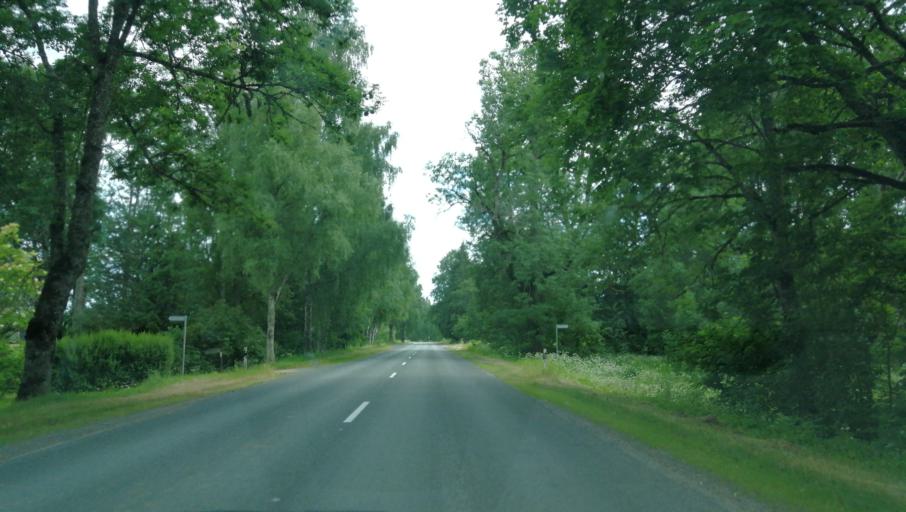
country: LV
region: Valmieras Rajons
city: Valmiera
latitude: 57.6626
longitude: 25.4289
